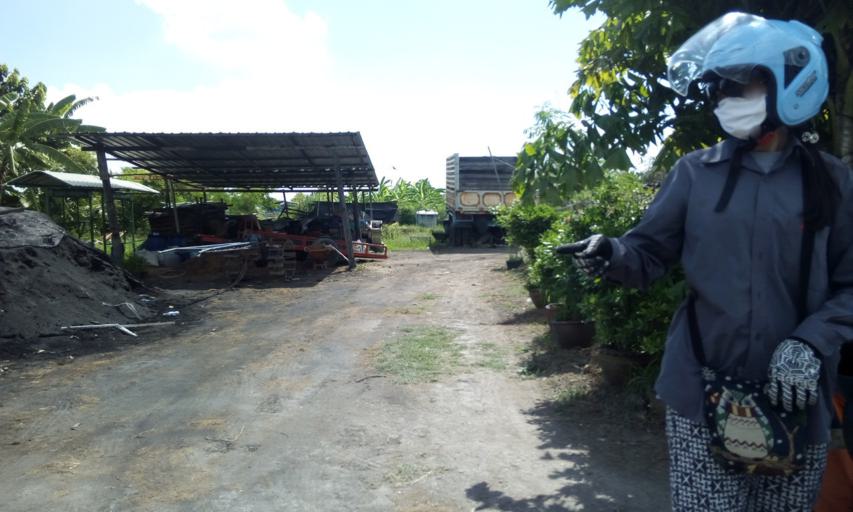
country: TH
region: Nakhon Nayok
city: Ongkharak
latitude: 14.0897
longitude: 100.9142
